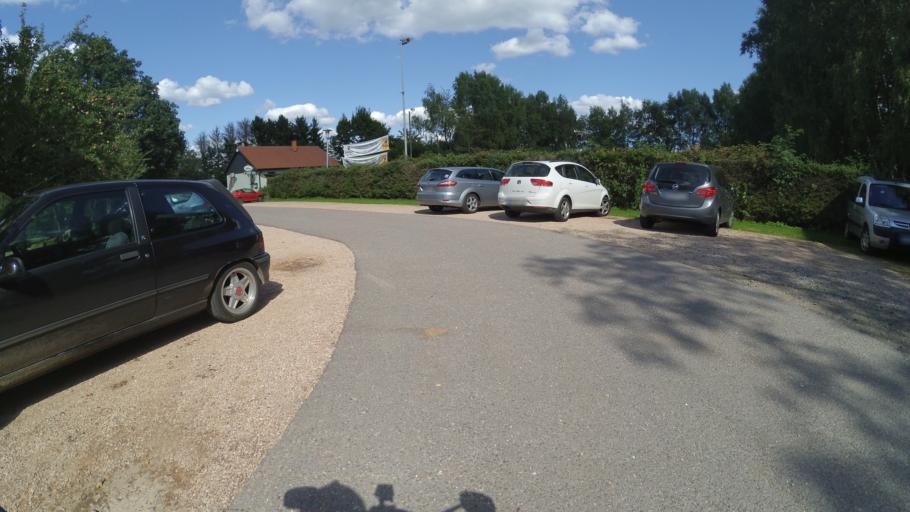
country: DE
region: Saarland
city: Marpingen
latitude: 49.4272
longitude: 7.0645
